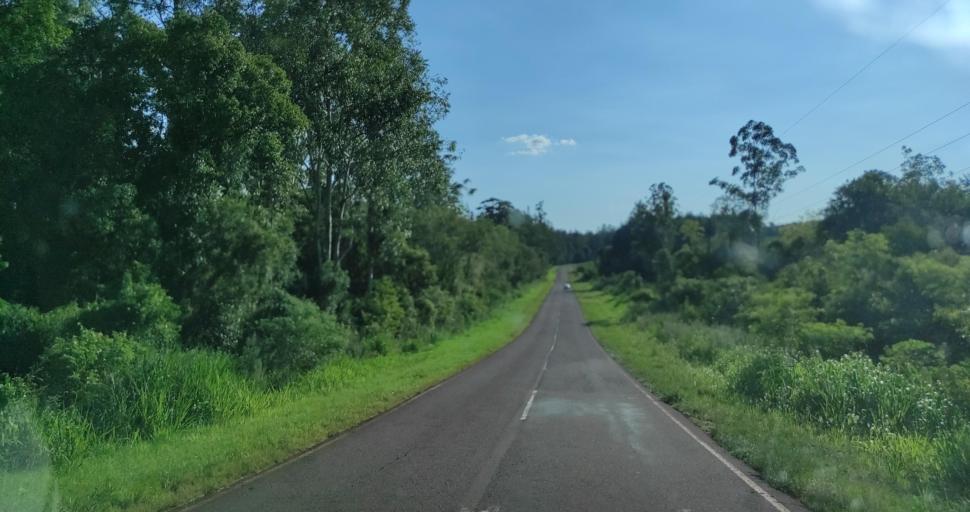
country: AR
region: Misiones
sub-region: Departamento de Eldorado
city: Eldorado
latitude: -26.3962
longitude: -54.3677
